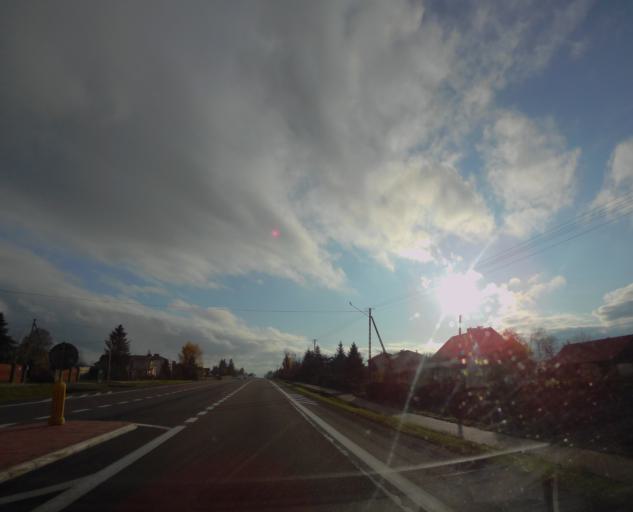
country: PL
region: Subcarpathian Voivodeship
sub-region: Powiat przemyski
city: Orly
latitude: 49.8666
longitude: 22.8094
